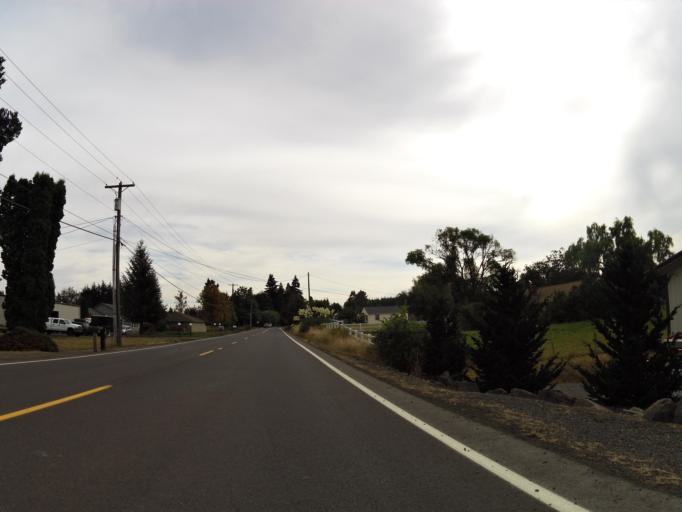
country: US
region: Washington
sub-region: Cowlitz County
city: West Side Highway
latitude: 46.2213
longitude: -122.8952
